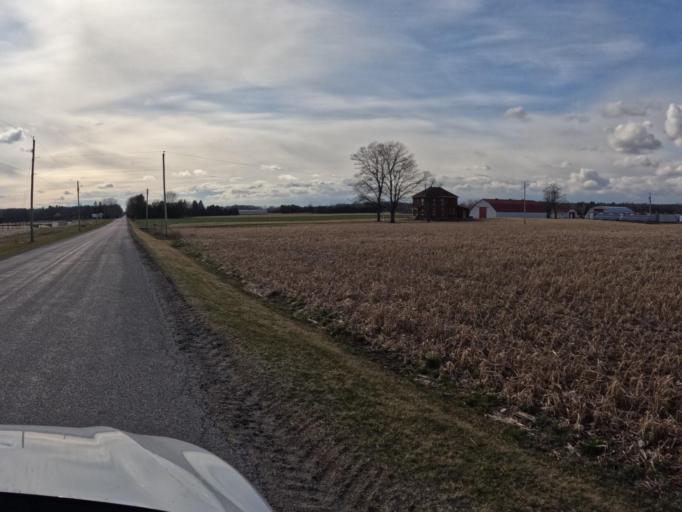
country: CA
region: Ontario
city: Brant
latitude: 42.9949
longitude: -80.3957
